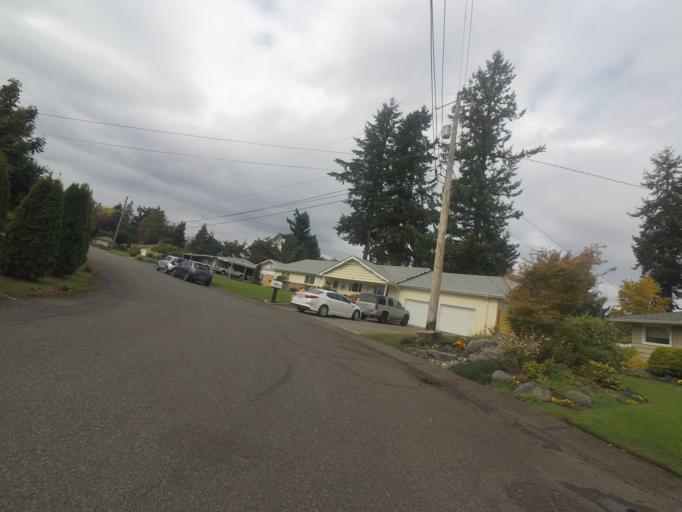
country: US
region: Washington
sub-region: Pierce County
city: University Place
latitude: 47.2149
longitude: -122.5403
